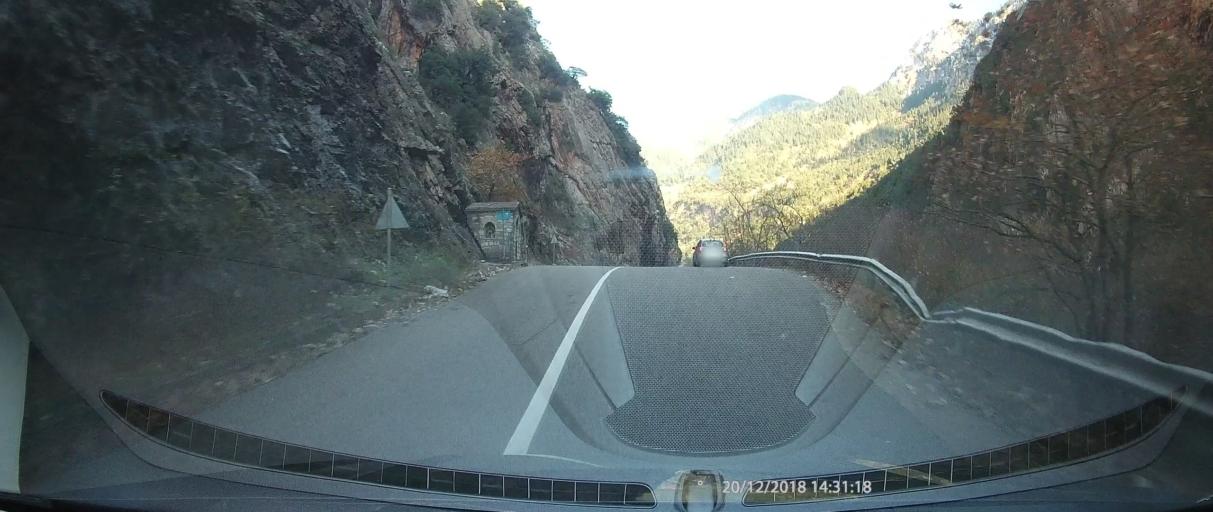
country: GR
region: Central Greece
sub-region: Nomos Evrytanias
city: Karpenisi
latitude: 38.7937
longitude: 21.7050
